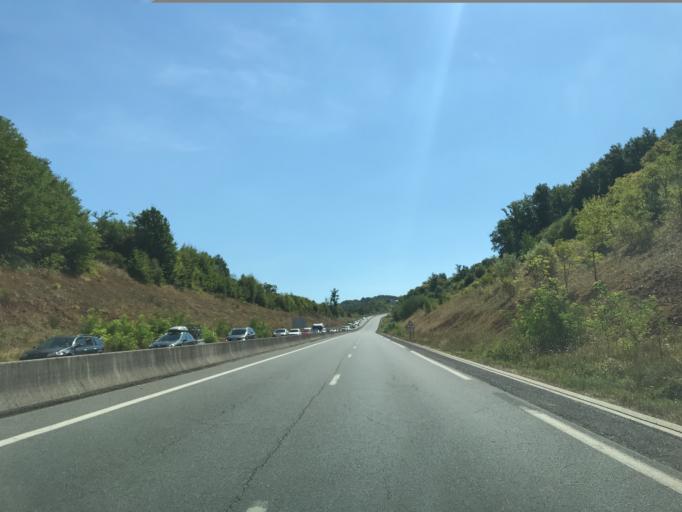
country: FR
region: Limousin
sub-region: Departement de la Correze
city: Ussac
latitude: 45.2010
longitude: 1.5130
